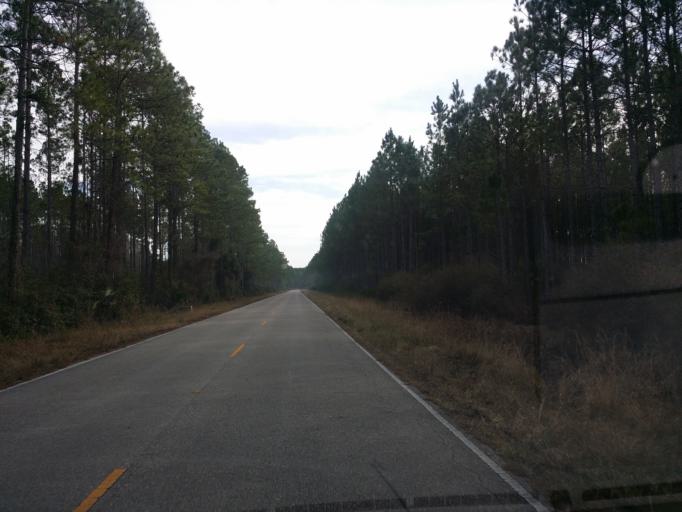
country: US
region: Florida
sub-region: Leon County
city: Woodville
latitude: 30.1817
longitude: -84.1649
